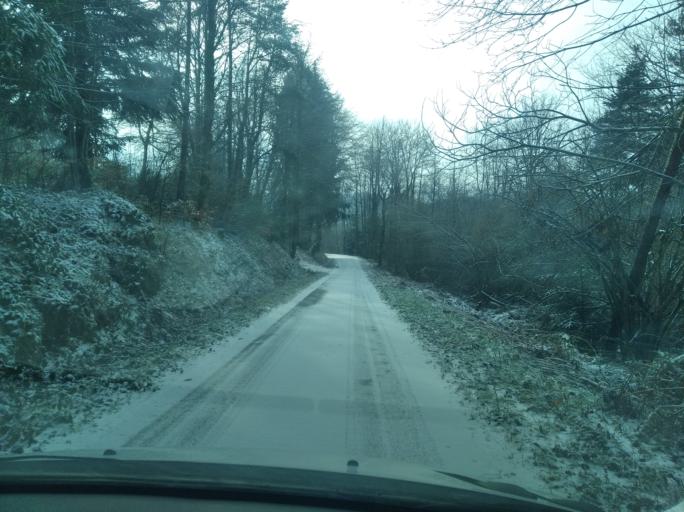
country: FR
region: Rhone-Alpes
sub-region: Departement de la Loire
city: La Pacaudiere
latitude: 46.1376
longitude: 3.7889
